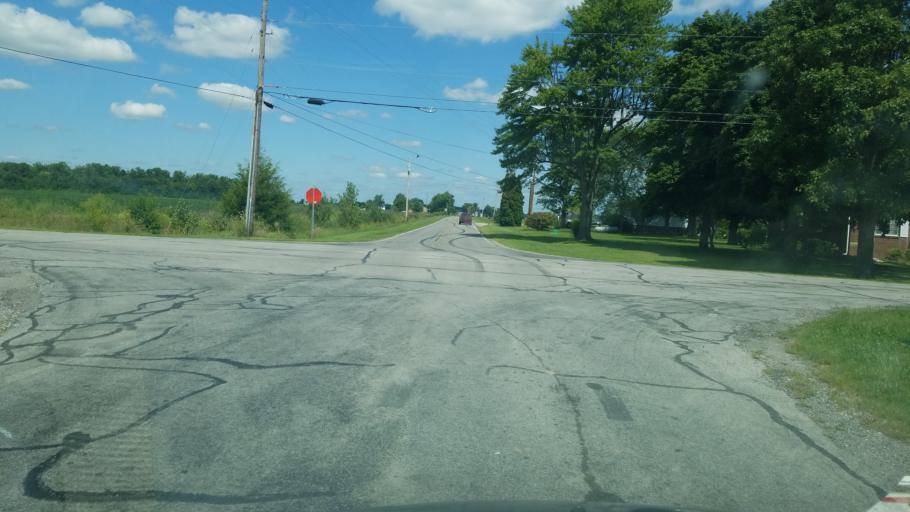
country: US
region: Ohio
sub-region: Fulton County
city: Swanton
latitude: 41.5881
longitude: -83.9407
